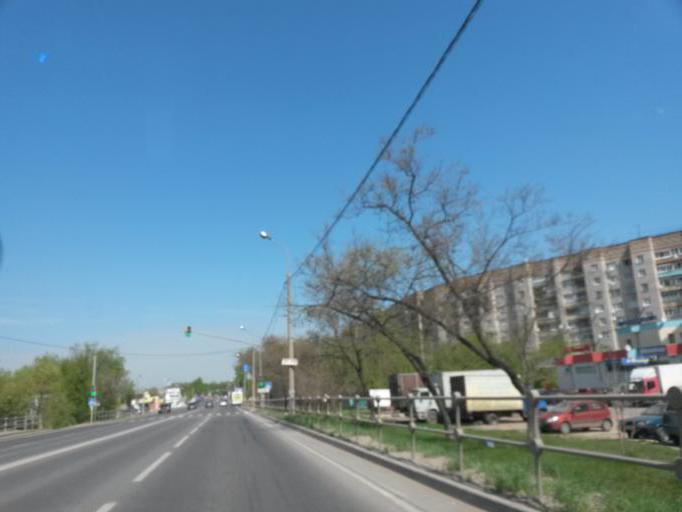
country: RU
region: Moskovskaya
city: Klimovsk
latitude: 55.3617
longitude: 37.5314
